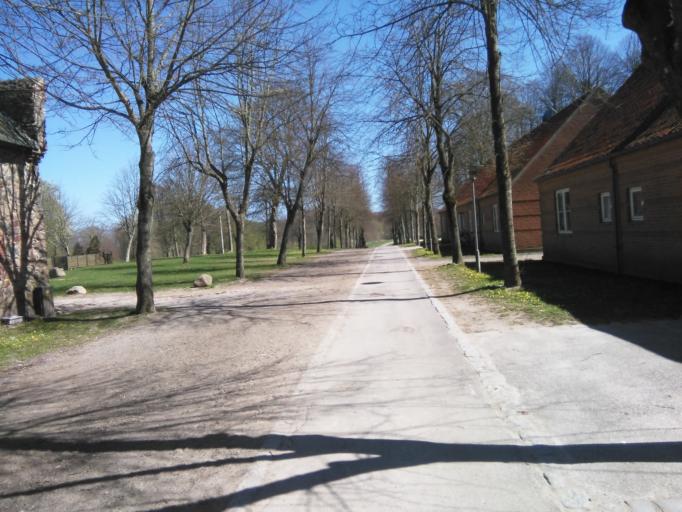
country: DK
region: Central Jutland
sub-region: Arhus Kommune
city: Marslet
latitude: 56.0664
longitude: 10.1872
